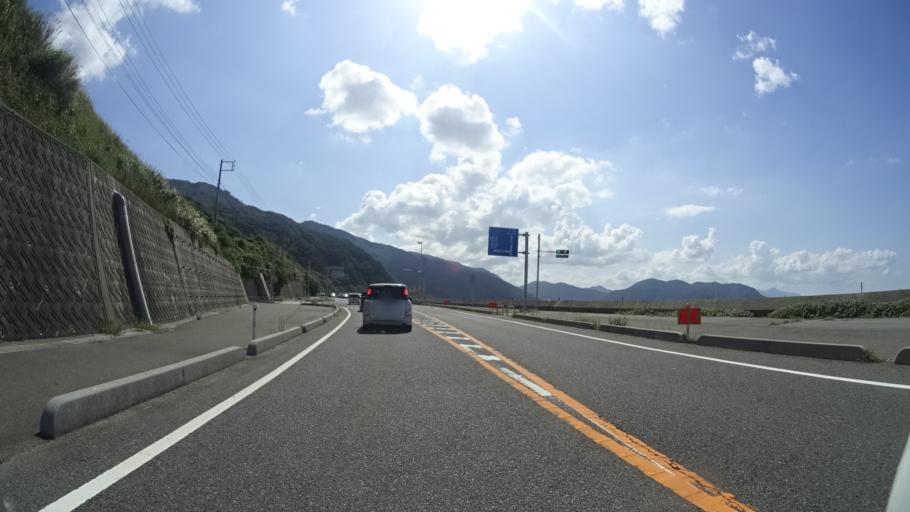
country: JP
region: Yamaguchi
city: Shimonoseki
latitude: 34.2457
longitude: 130.9121
